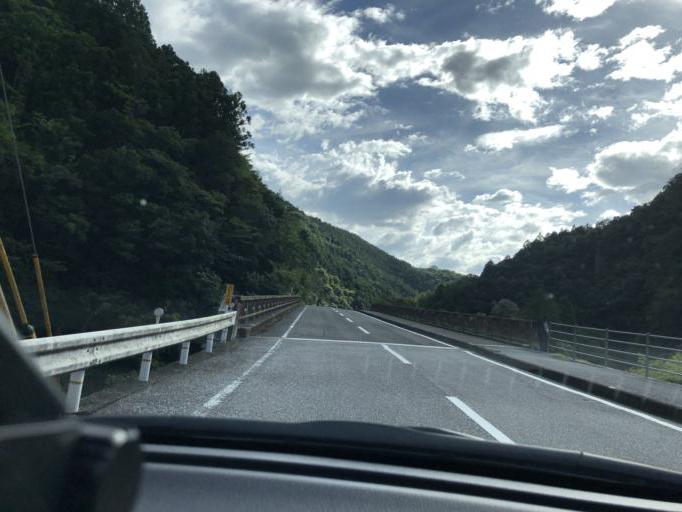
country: JP
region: Kochi
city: Kochi-shi
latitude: 33.6303
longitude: 133.5163
